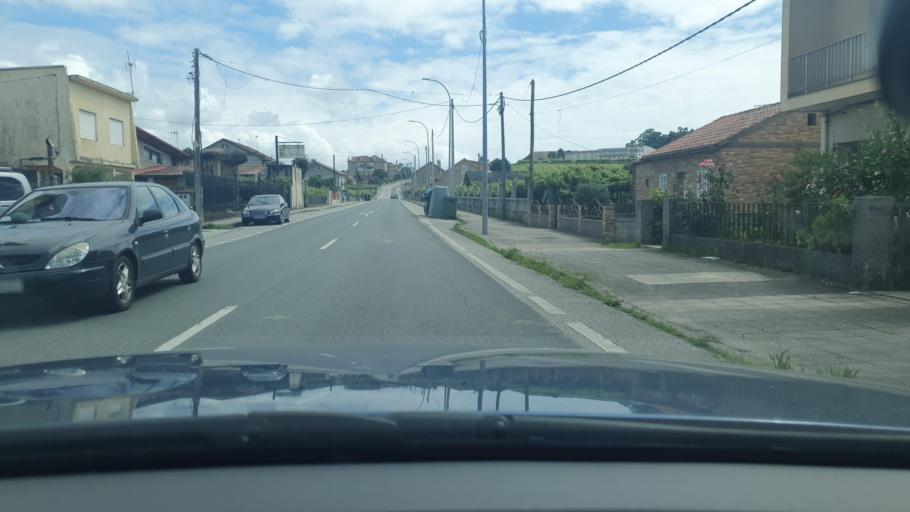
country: ES
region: Galicia
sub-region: Provincia de Pontevedra
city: Cambados
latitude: 42.4948
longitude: -8.8029
